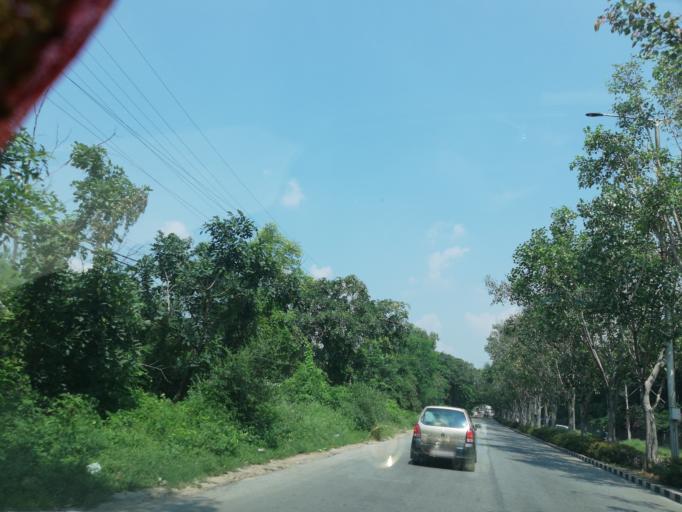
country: IN
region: Telangana
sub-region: Medak
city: Serilingampalle
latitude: 17.4665
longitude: 78.3326
